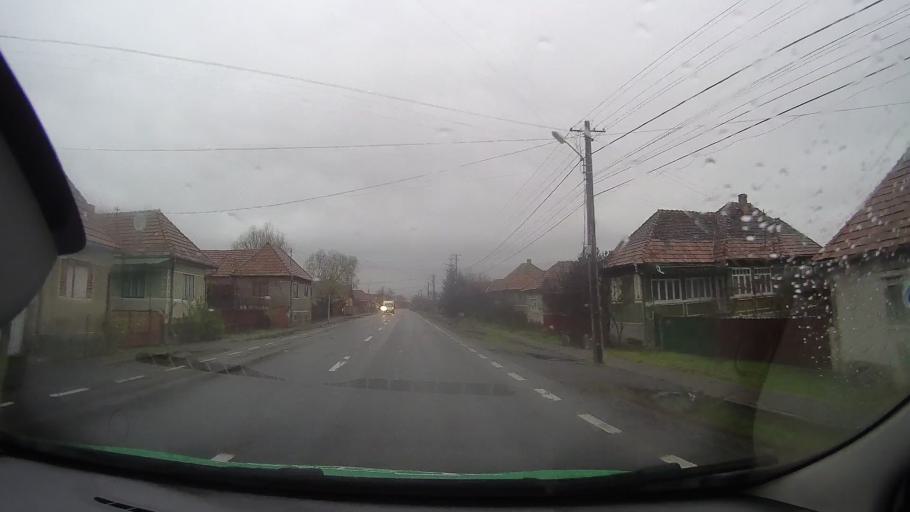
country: RO
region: Mures
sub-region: Comuna Brancovenesti
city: Valenii de Mures
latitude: 46.8841
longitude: 24.7867
